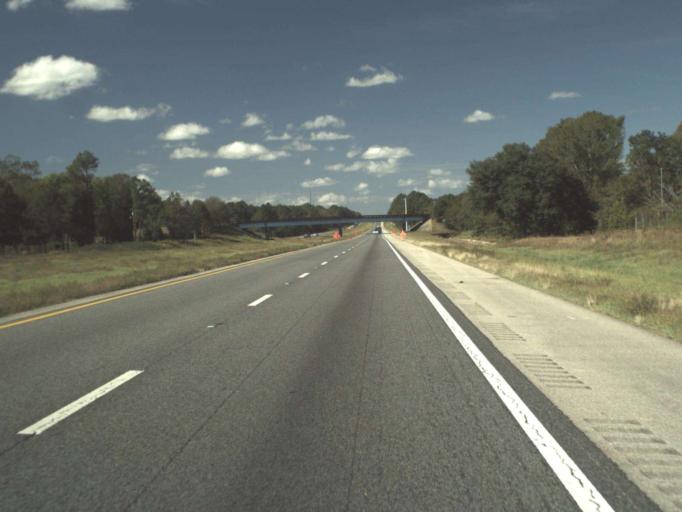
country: US
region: Florida
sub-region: Washington County
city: Chipley
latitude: 30.7464
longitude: -85.5055
